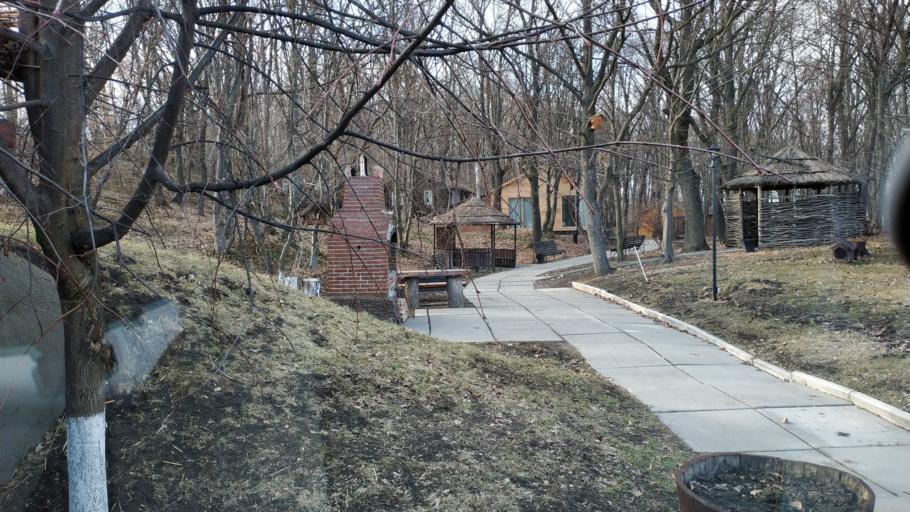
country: MD
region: Calarasi
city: Calarasi
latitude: 47.3326
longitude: 28.0877
